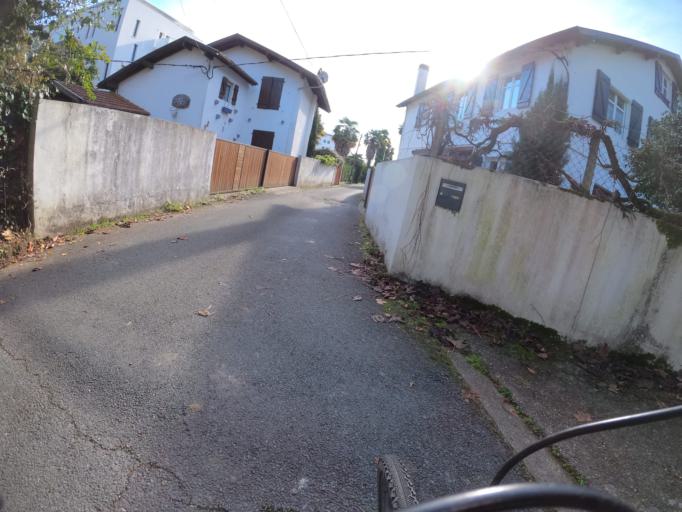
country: FR
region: Aquitaine
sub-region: Departement des Pyrenees-Atlantiques
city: Bayonne
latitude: 43.4986
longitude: -1.4644
